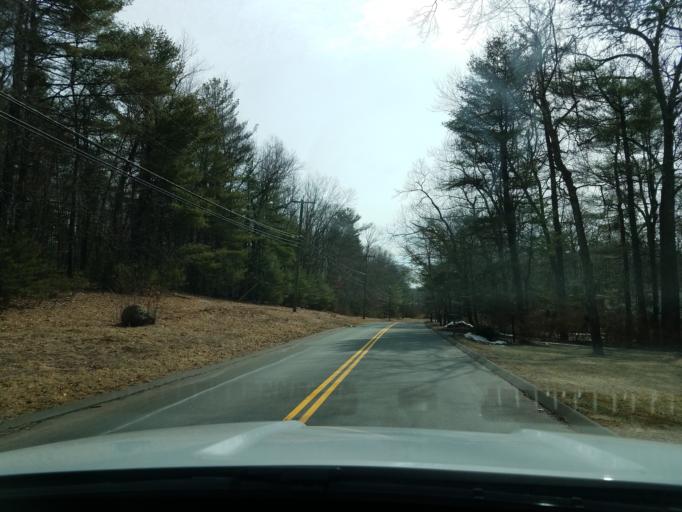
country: US
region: Connecticut
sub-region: Hartford County
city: Collinsville
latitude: 41.7805
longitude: -72.9168
